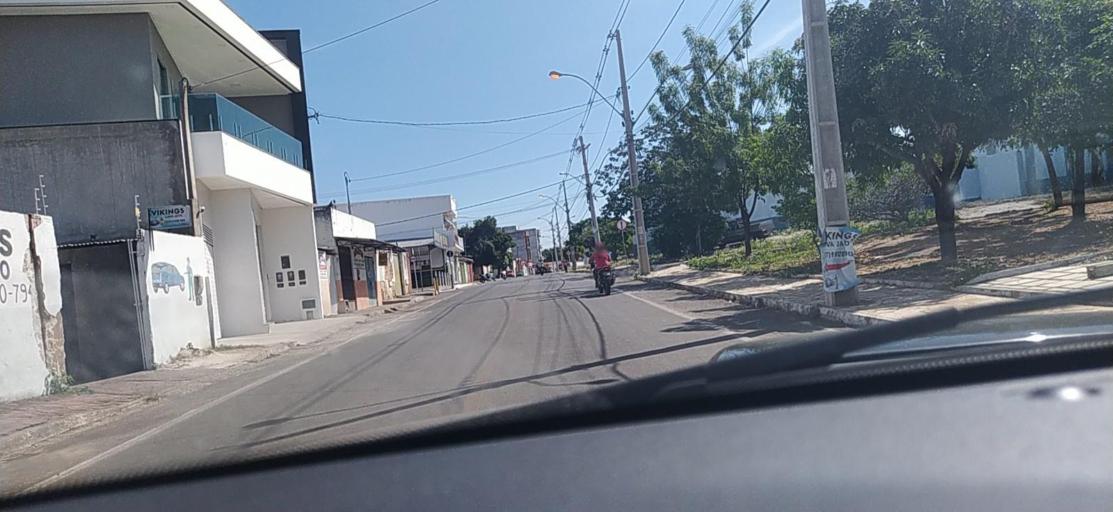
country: BR
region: Bahia
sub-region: Guanambi
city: Guanambi
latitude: -14.2181
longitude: -42.7721
